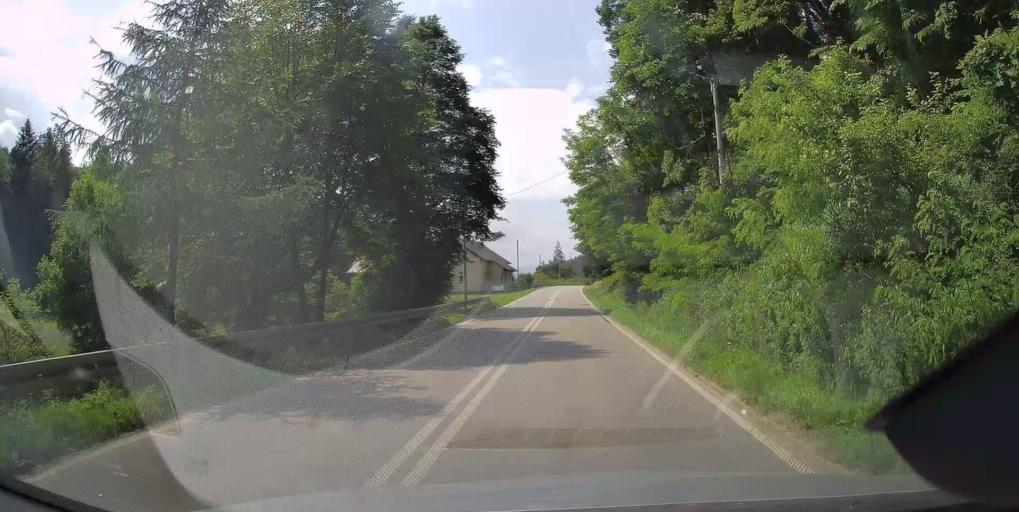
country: PL
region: Lesser Poland Voivodeship
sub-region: Powiat nowosadecki
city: Nowy Sacz
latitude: 49.6553
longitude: 20.7251
